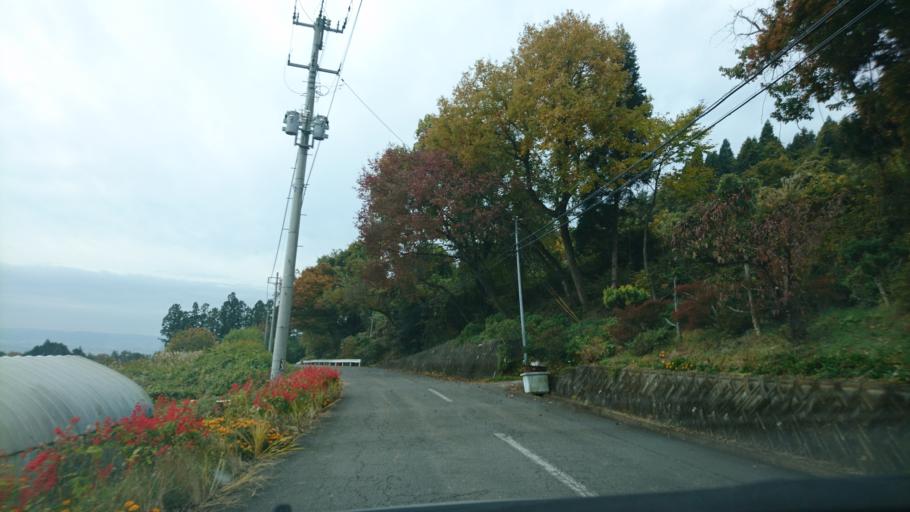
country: JP
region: Iwate
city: Ichinoseki
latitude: 38.9790
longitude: 141.1690
